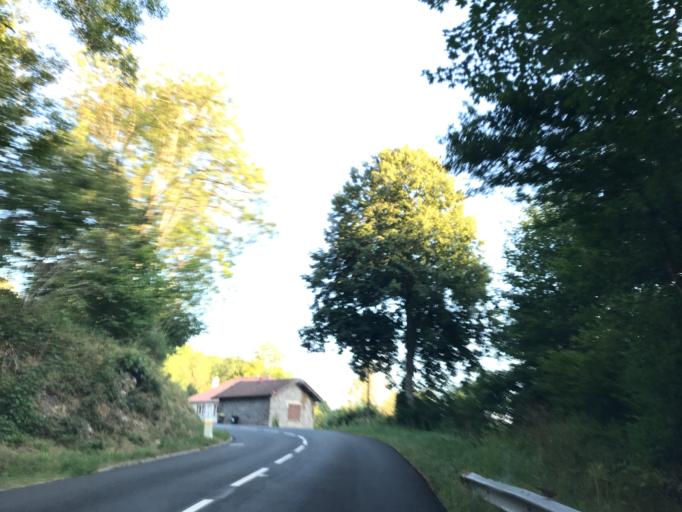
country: FR
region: Auvergne
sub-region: Departement du Puy-de-Dome
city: Saint-Remy-sur-Durolle
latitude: 45.8950
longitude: 3.5870
